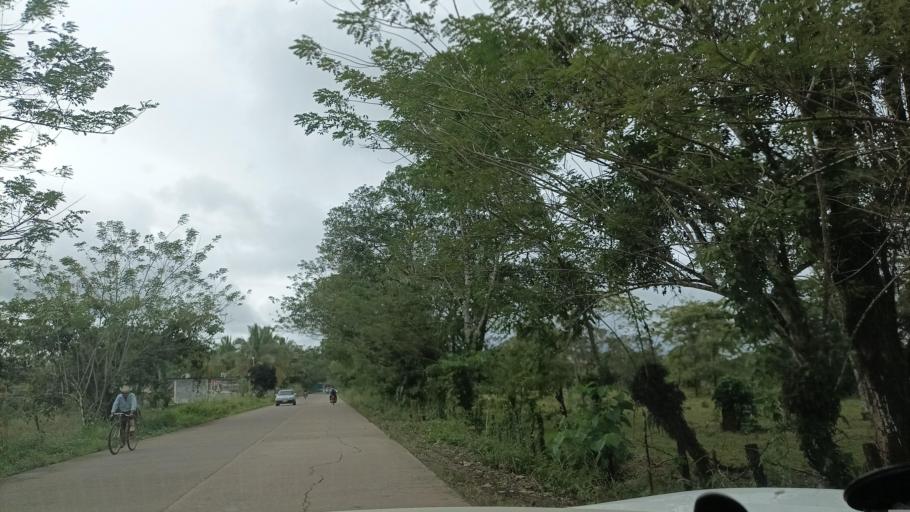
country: MX
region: Veracruz
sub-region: Uxpanapa
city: Poblado 10
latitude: 17.2771
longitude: -94.4608
